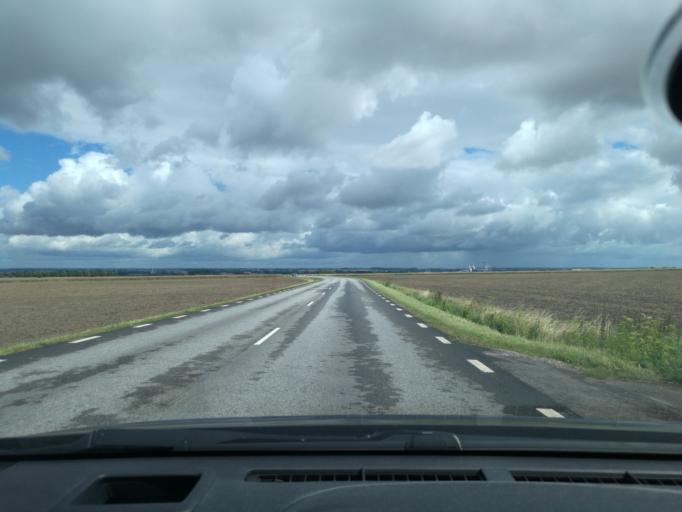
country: SE
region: Skane
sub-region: Lunds Kommun
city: Lund
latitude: 55.7577
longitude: 13.2222
